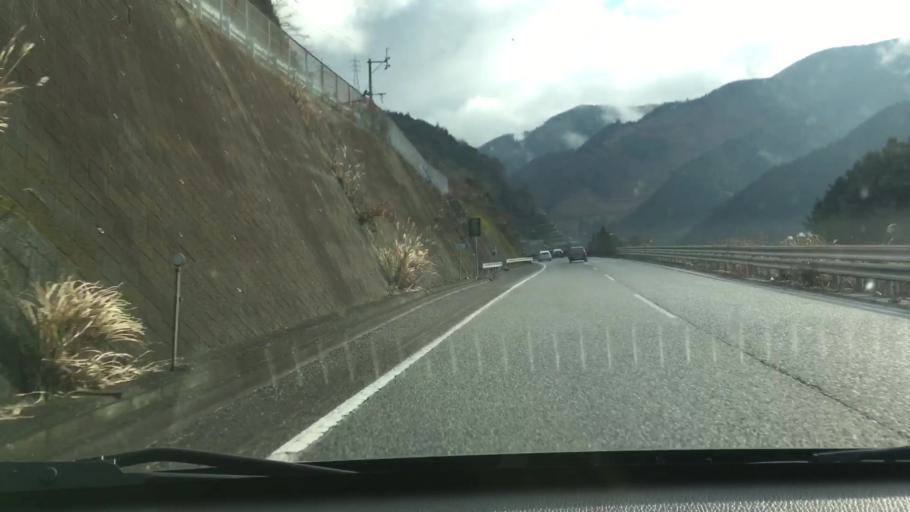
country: JP
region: Kumamoto
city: Yatsushiro
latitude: 32.4088
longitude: 130.6968
